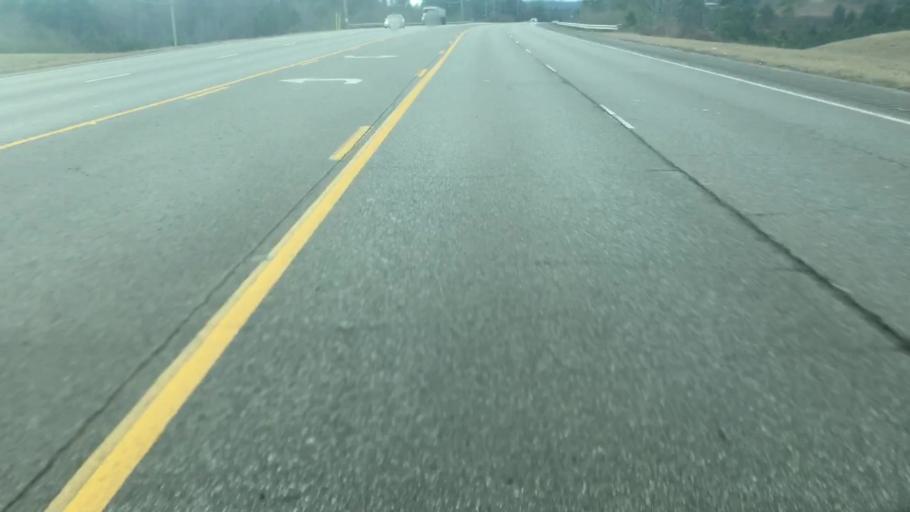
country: US
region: Alabama
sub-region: Walker County
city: Jasper
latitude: 33.8034
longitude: -87.2356
